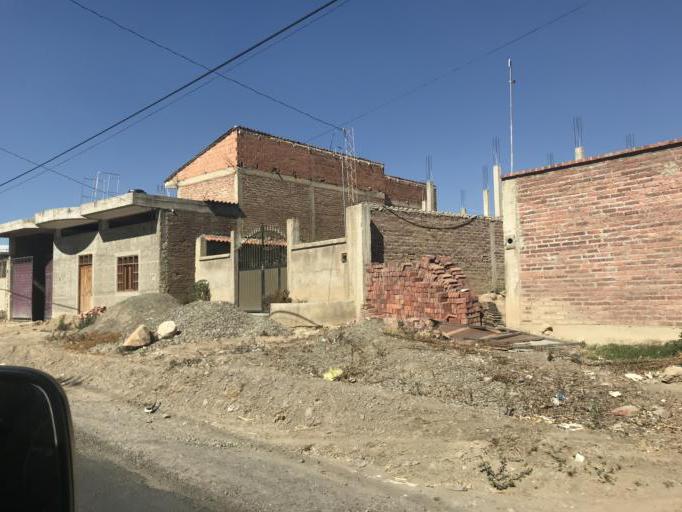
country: BO
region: Cochabamba
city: Punata
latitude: -17.5566
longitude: -65.8611
